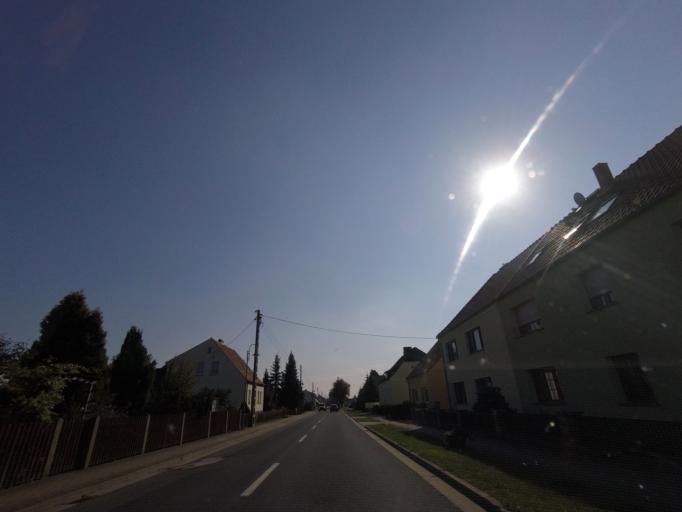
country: DE
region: Saxony-Anhalt
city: Jessen
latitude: 51.8575
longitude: 13.0252
